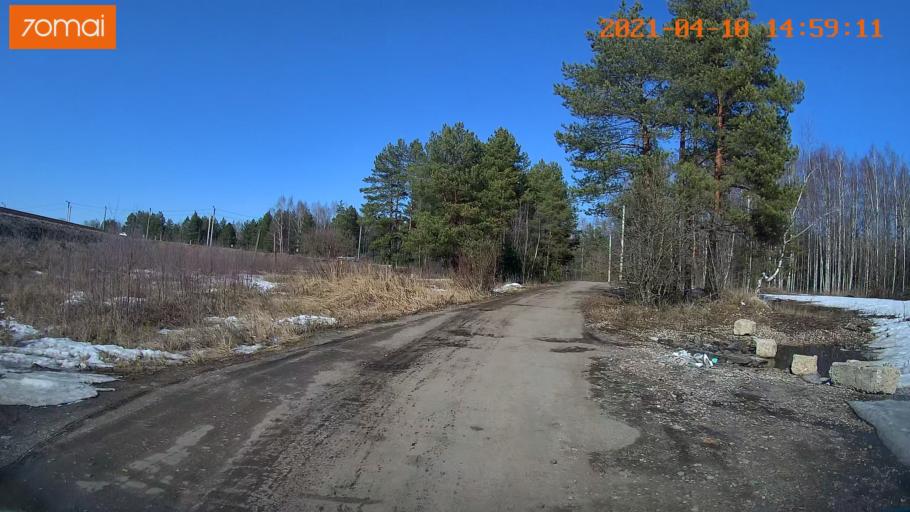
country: RU
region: Ivanovo
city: Bogorodskoye
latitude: 56.9968
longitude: 41.0601
